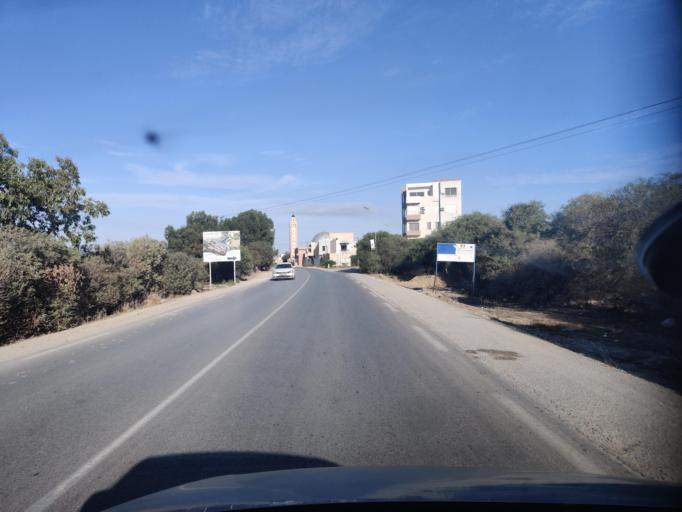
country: TN
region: Ariana
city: Ariana
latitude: 36.9535
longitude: 10.2328
